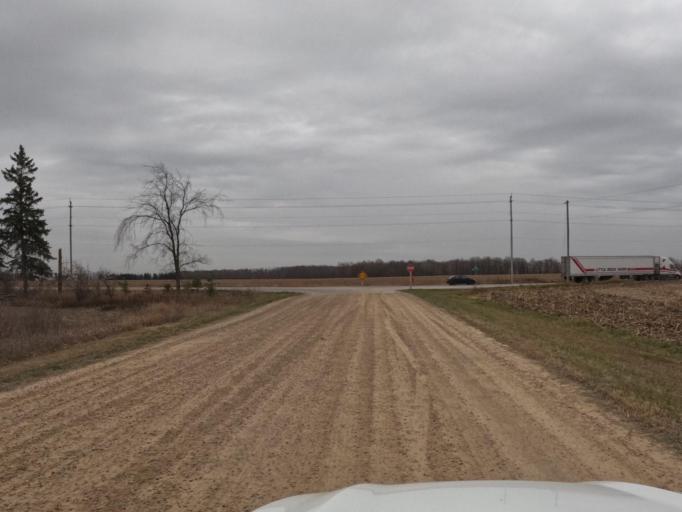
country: CA
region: Ontario
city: Orangeville
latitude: 43.8660
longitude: -80.3546
